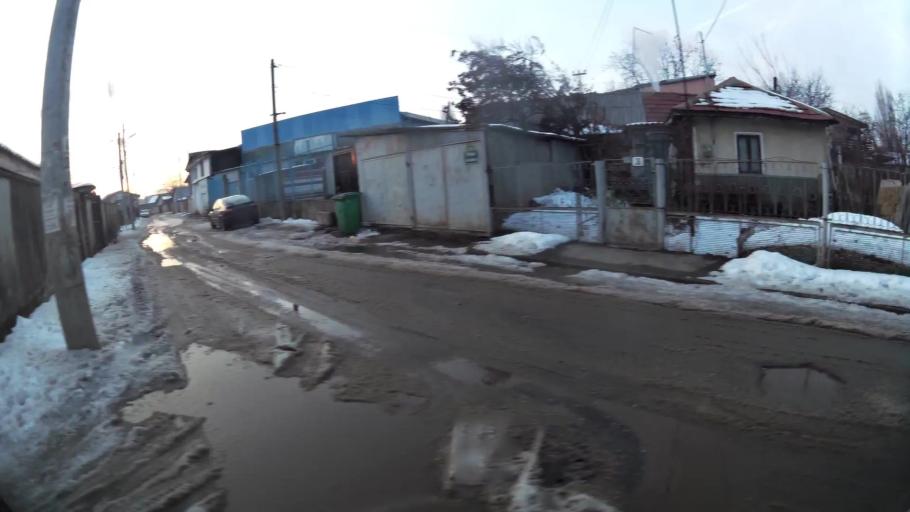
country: RO
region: Ilfov
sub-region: Comuna Magurele
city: Magurele
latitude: 44.3904
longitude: 26.0216
